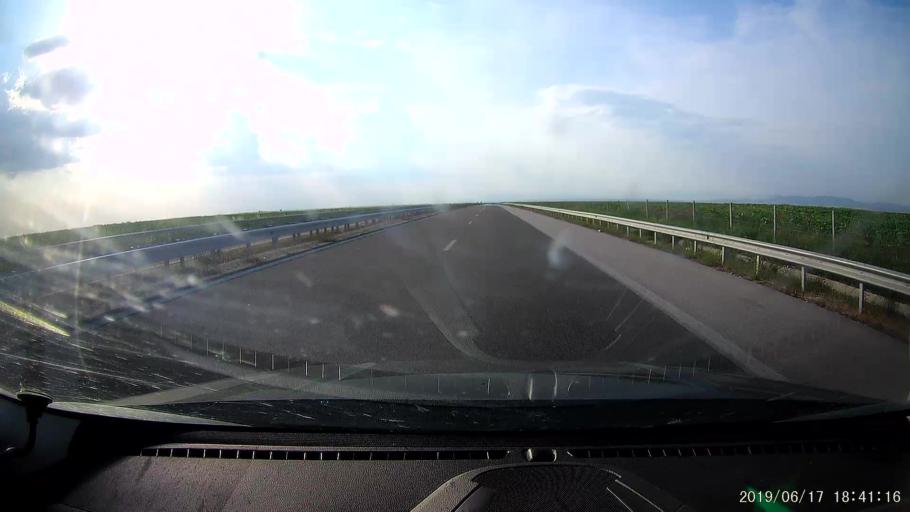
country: BG
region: Stara Zagora
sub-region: Obshtina Chirpan
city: Chirpan
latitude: 42.1691
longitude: 25.2588
